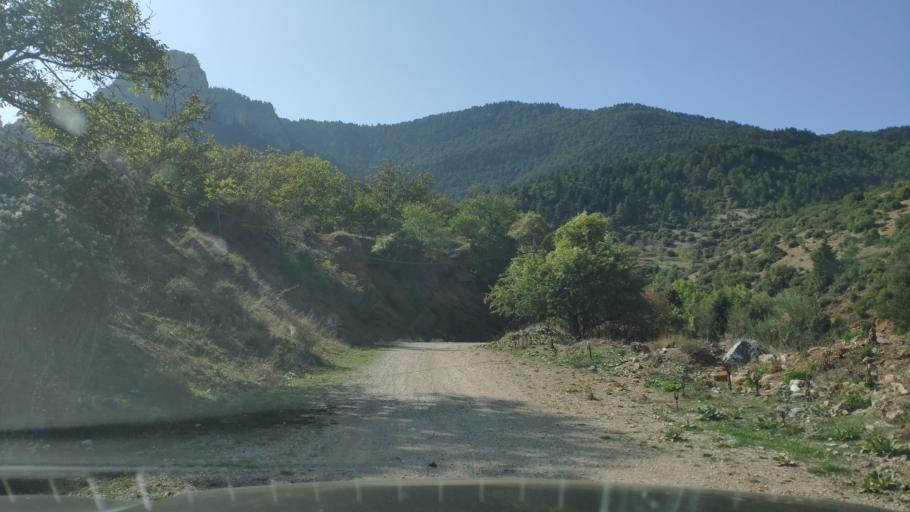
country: GR
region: West Greece
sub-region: Nomos Achaias
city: Aiyira
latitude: 37.9923
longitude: 22.3540
